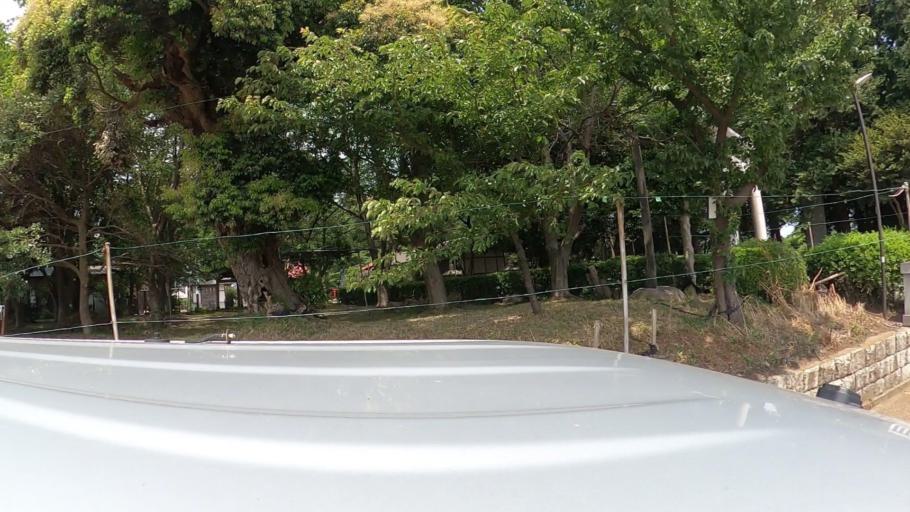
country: JP
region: Kanagawa
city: Chigasaki
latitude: 35.3914
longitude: 139.4215
